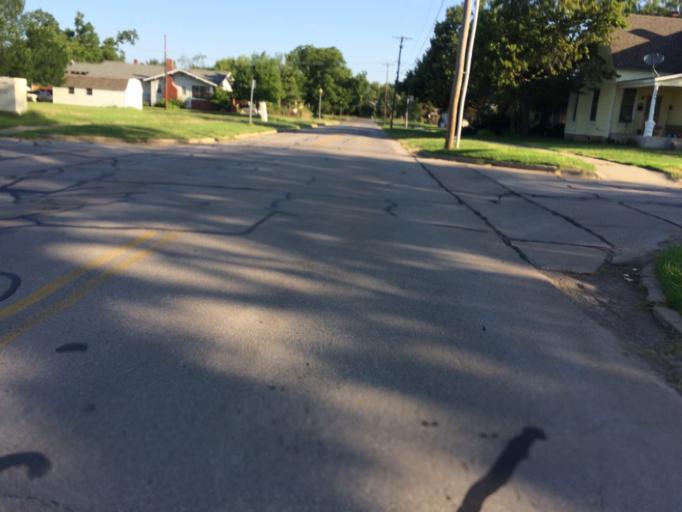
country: US
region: Oklahoma
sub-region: Cleveland County
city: Norman
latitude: 35.2242
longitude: -97.4436
